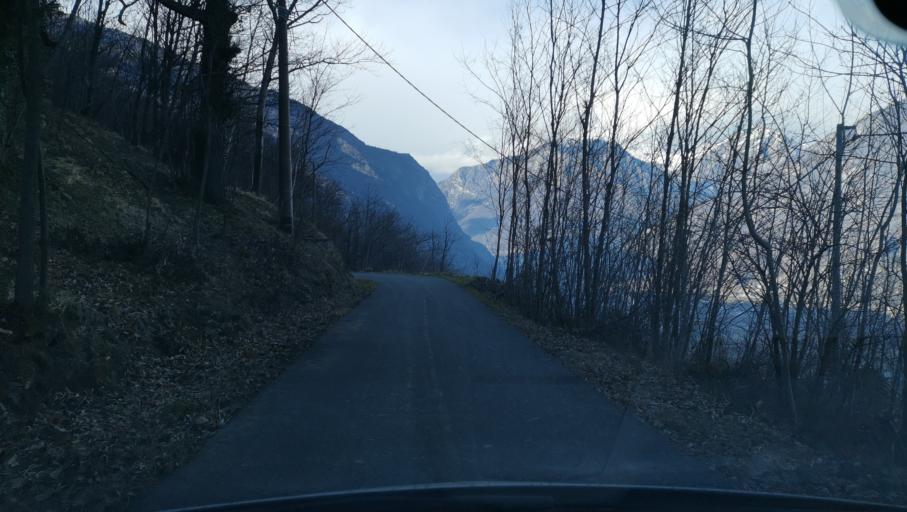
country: IT
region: Piedmont
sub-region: Provincia di Torino
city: Tavagnasco
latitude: 45.5446
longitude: 7.8161
